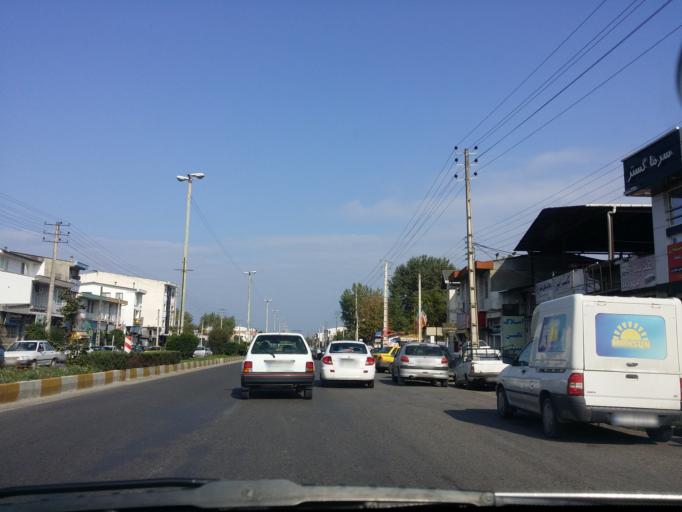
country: IR
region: Mazandaran
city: Chalus
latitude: 36.6740
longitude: 51.4058
